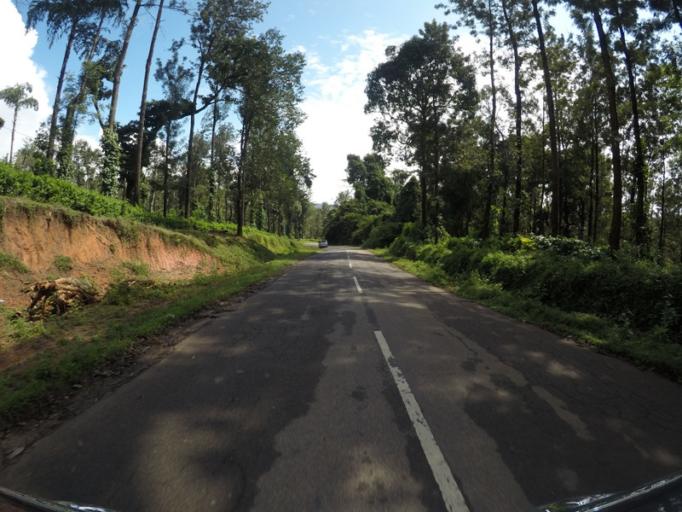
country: IN
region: Karnataka
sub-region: Kodagu
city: Suntikoppa
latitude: 12.5039
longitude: 75.7999
